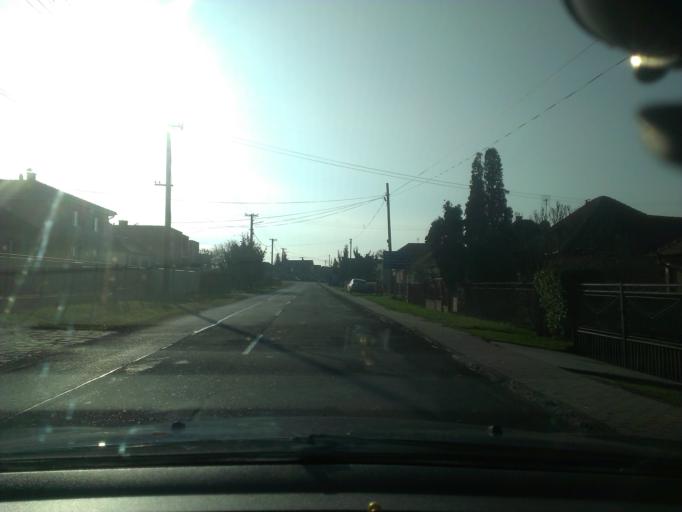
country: SK
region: Trnavsky
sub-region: Okres Trnava
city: Piestany
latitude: 48.5079
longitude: 17.9852
